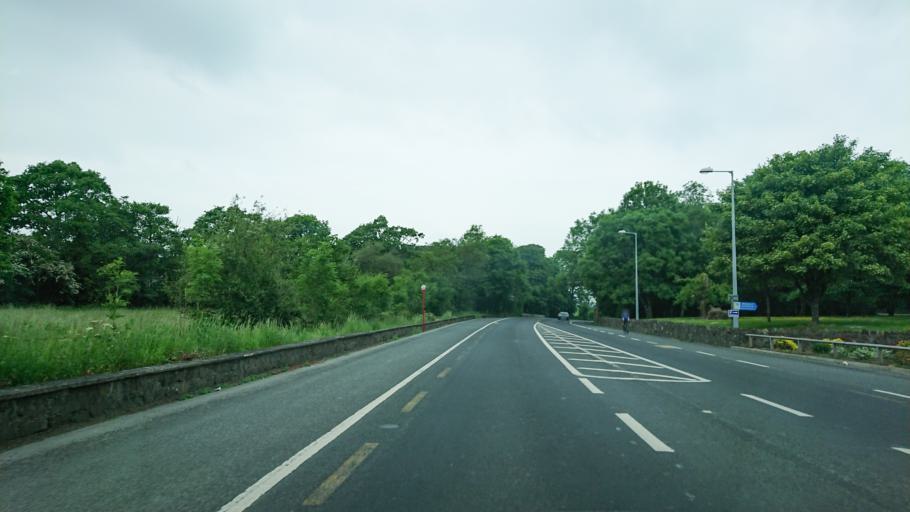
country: IE
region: Munster
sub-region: Waterford
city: Waterford
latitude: 52.2138
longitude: -7.1220
